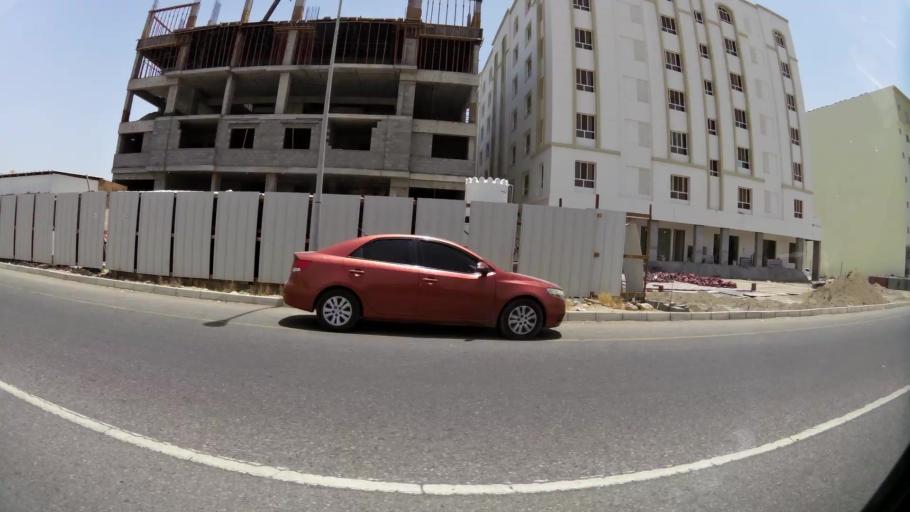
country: OM
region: Muhafazat Masqat
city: Bawshar
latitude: 23.5575
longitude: 58.4103
